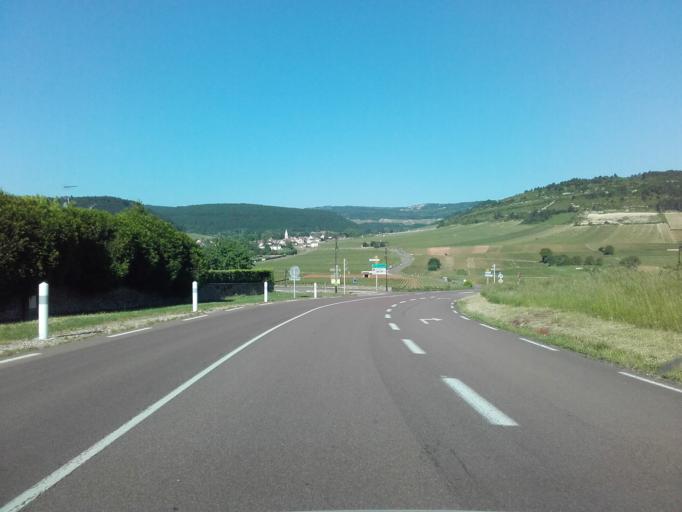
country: FR
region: Bourgogne
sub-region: Departement de la Cote-d'Or
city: Meursault
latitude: 46.9886
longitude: 4.7680
